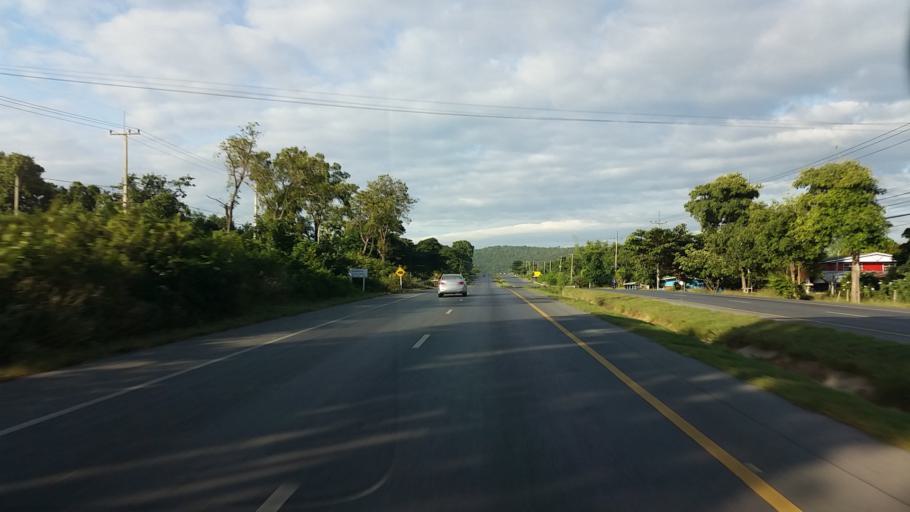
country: TH
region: Lop Buri
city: Phatthana Nikhom
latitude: 14.9837
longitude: 100.9196
